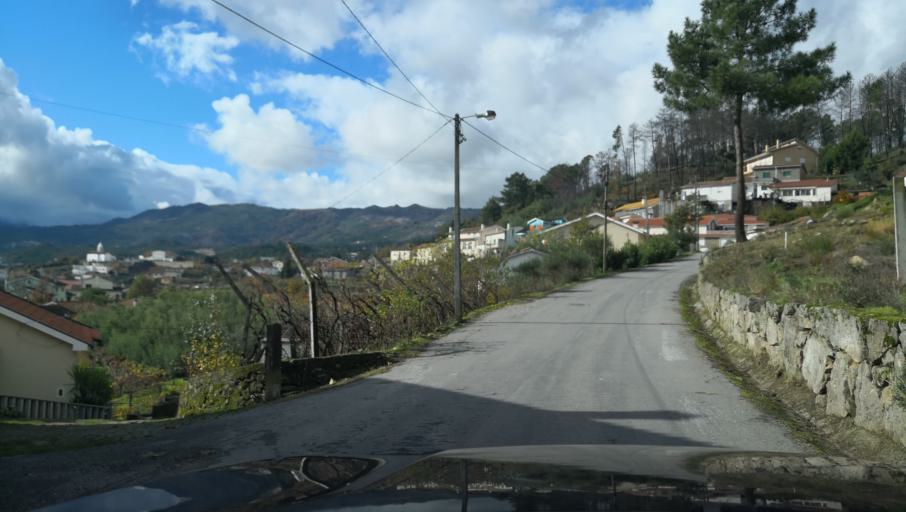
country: PT
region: Vila Real
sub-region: Vila Real
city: Vila Real
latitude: 41.3225
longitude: -7.7598
